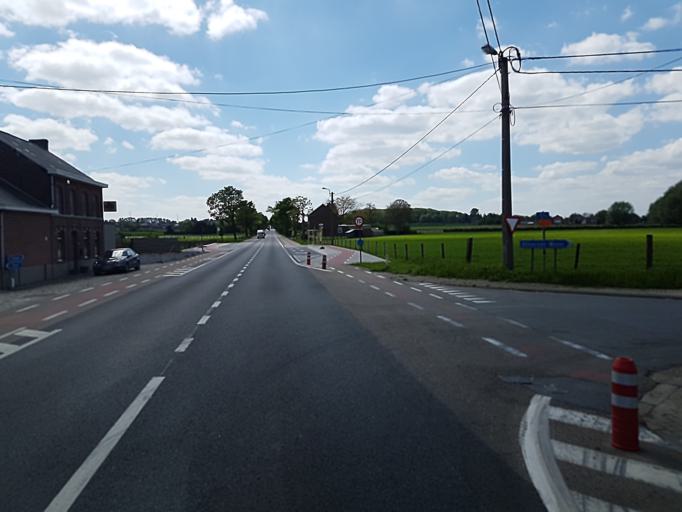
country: BE
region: Flanders
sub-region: Provincie Vlaams-Brabant
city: Glabbeek-Zuurbemde
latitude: 50.8556
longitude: 4.9528
